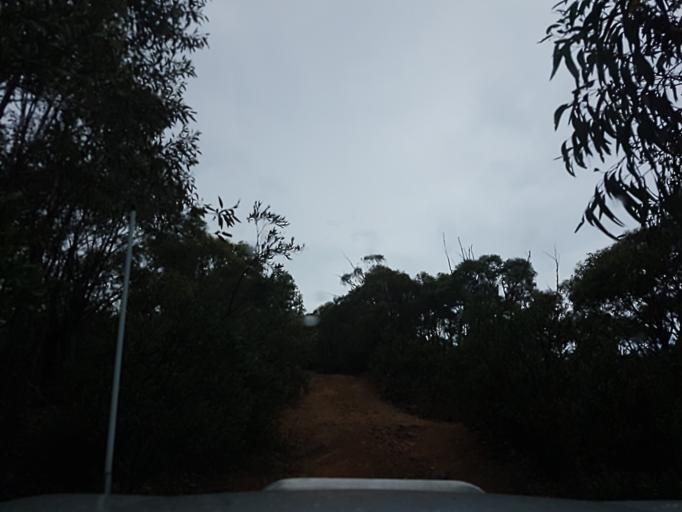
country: AU
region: New South Wales
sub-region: Snowy River
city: Jindabyne
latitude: -36.9189
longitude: 148.3404
